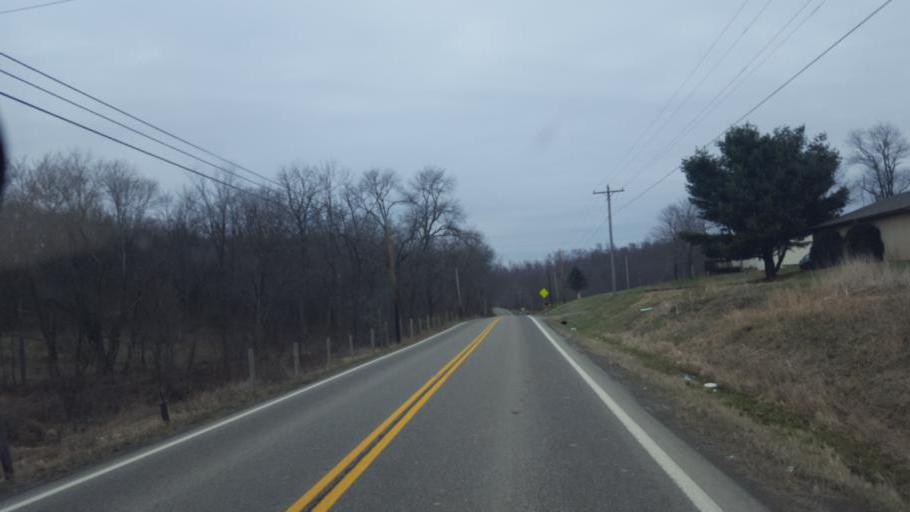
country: US
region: Ohio
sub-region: Tuscarawas County
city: Sugarcreek
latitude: 40.5803
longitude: -81.7084
